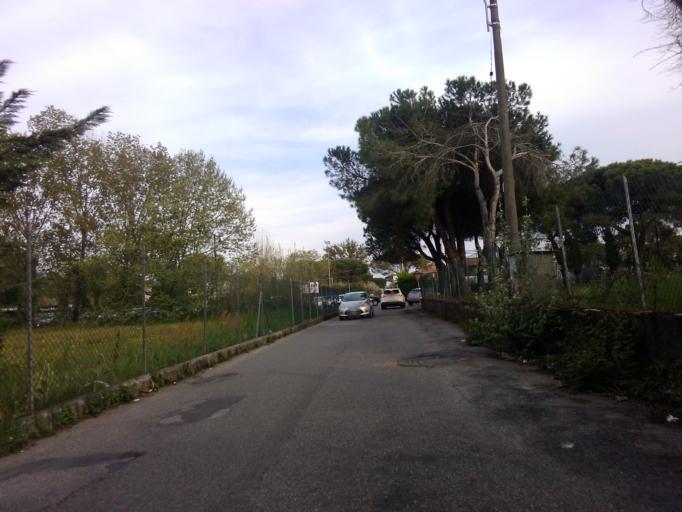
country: IT
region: Tuscany
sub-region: Provincia di Massa-Carrara
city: Massa
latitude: 44.0168
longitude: 10.0980
